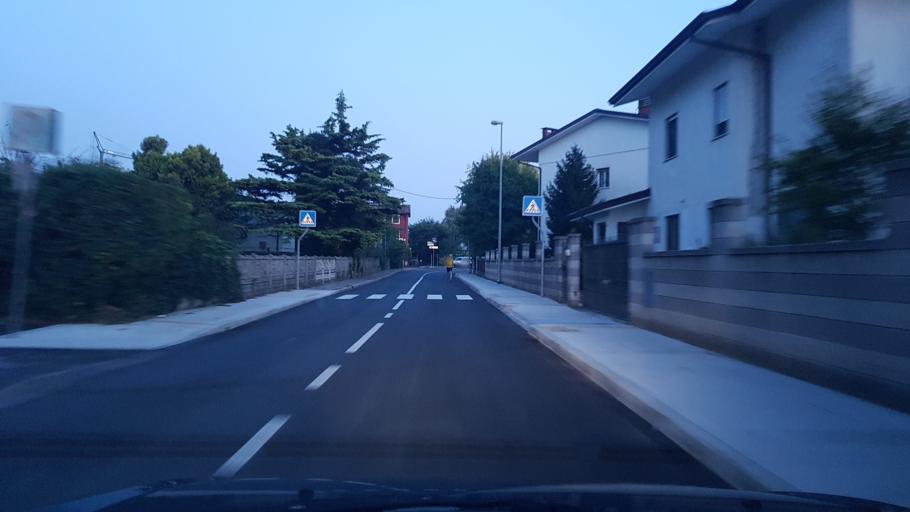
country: IT
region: Friuli Venezia Giulia
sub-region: Provincia di Gorizia
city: Staranzano
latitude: 45.8078
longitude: 13.4988
